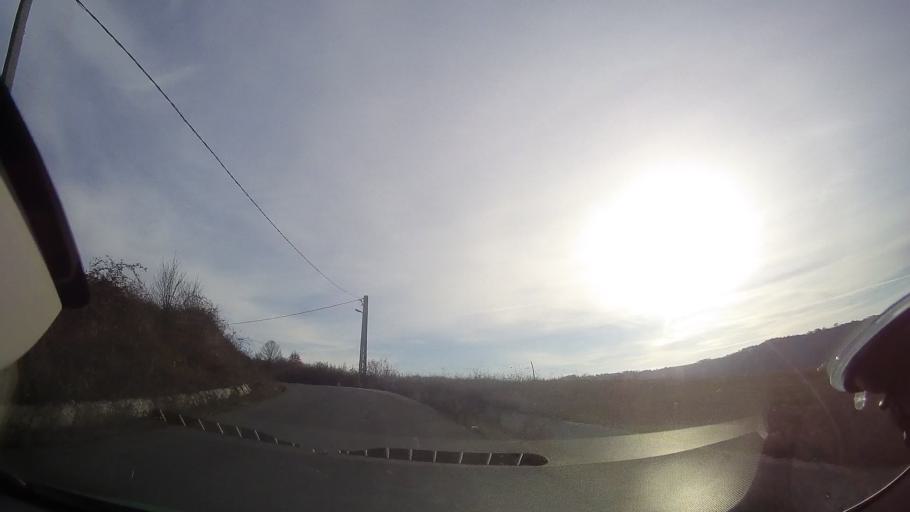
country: RO
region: Bihor
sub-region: Comuna Sarbi
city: Burzuc
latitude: 47.1370
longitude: 22.1836
